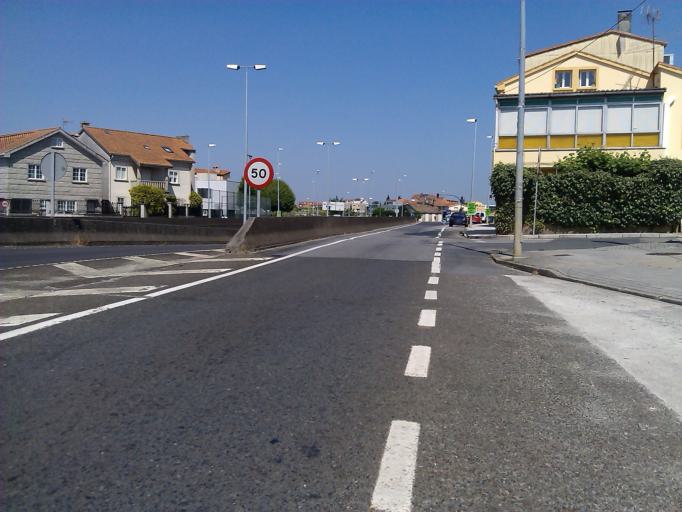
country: ES
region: Galicia
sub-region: Provincia da Coruna
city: Santiago de Compostela
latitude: 42.8589
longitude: -8.5383
